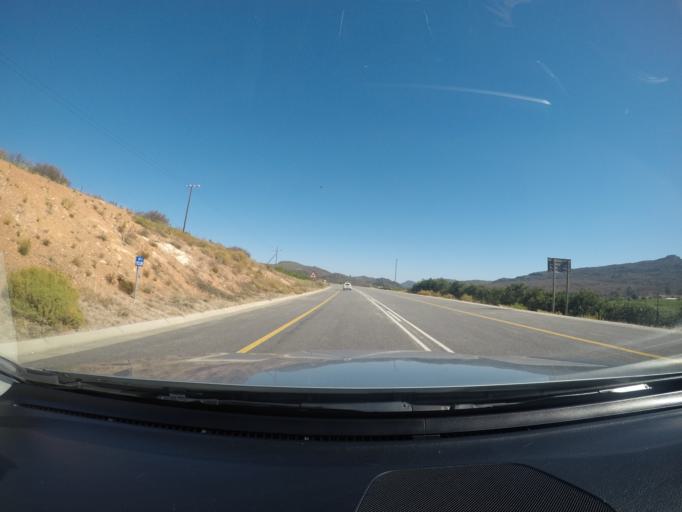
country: ZA
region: Western Cape
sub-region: West Coast District Municipality
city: Clanwilliam
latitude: -32.4416
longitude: 18.9582
